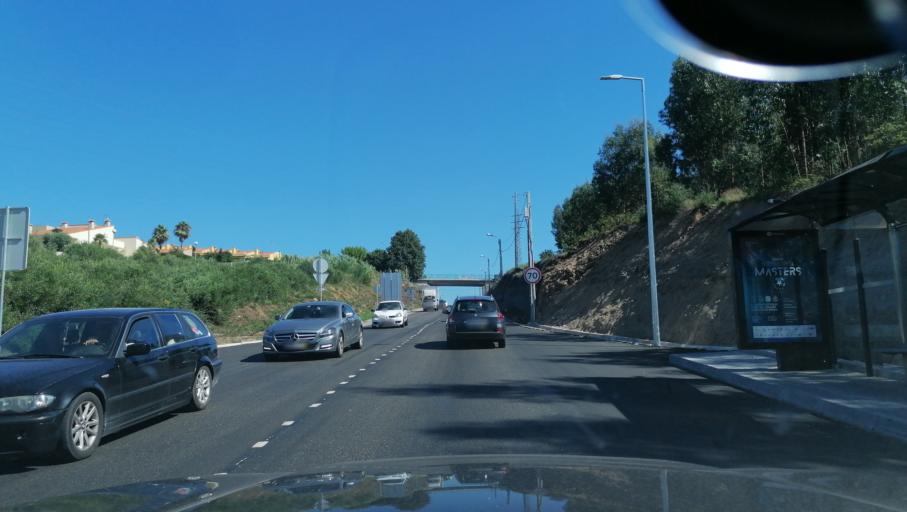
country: PT
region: Aveiro
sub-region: Santa Maria da Feira
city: Arrifana
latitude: 40.9289
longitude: -8.5110
